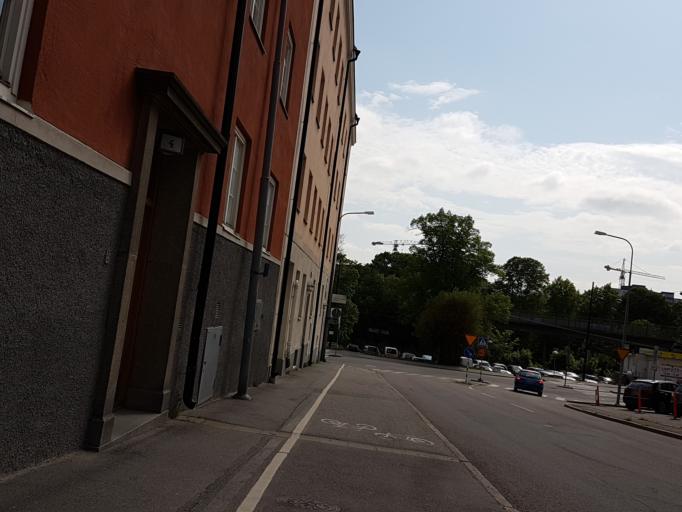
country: SE
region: Stockholm
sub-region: Sundbybergs Kommun
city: Sundbyberg
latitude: 59.3657
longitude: 17.9586
